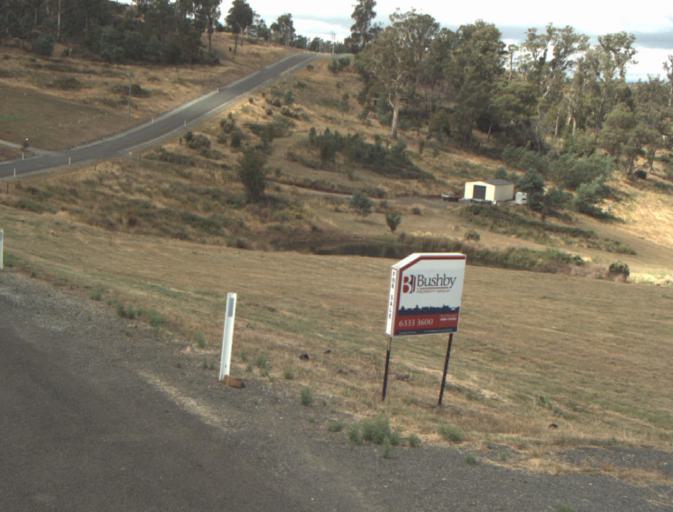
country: AU
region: Tasmania
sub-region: Launceston
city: Mayfield
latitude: -41.3024
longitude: 147.0417
